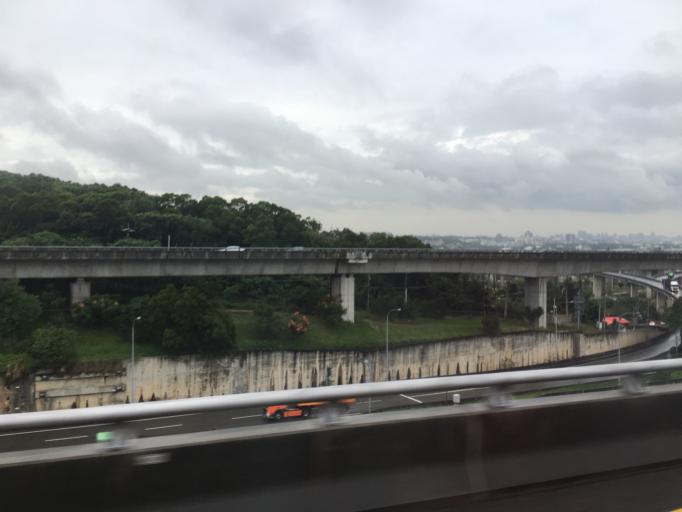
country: TW
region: Taiwan
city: Daxi
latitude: 24.9330
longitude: 121.1866
